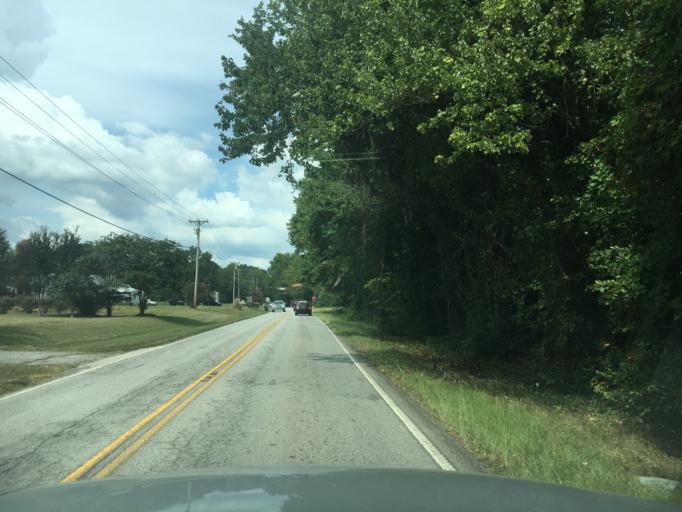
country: US
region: South Carolina
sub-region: Greenville County
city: Five Forks
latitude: 34.8211
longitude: -82.2288
